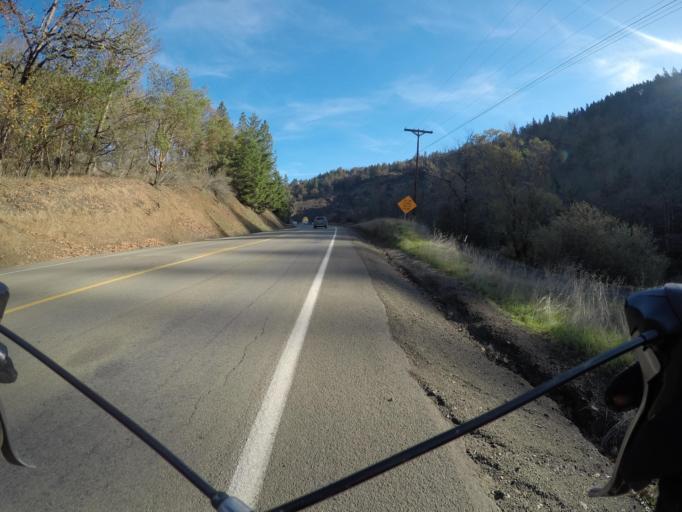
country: US
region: Oregon
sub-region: Douglas County
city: Winston
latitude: 43.1882
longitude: -123.4456
